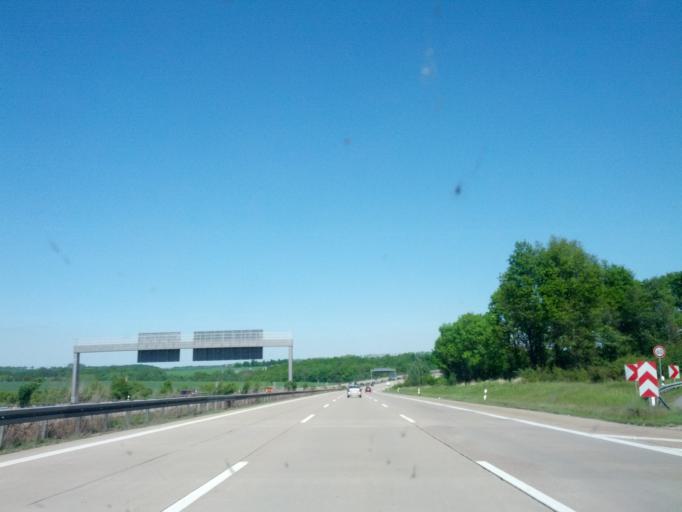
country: DE
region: Saxony
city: Reinsberg
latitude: 51.0553
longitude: 13.3711
